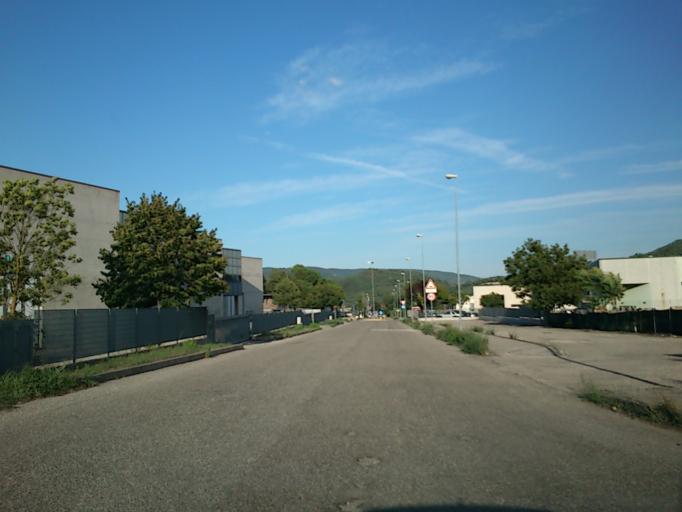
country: IT
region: The Marches
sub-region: Provincia di Pesaro e Urbino
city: Fermignano
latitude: 43.6897
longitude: 12.6467
